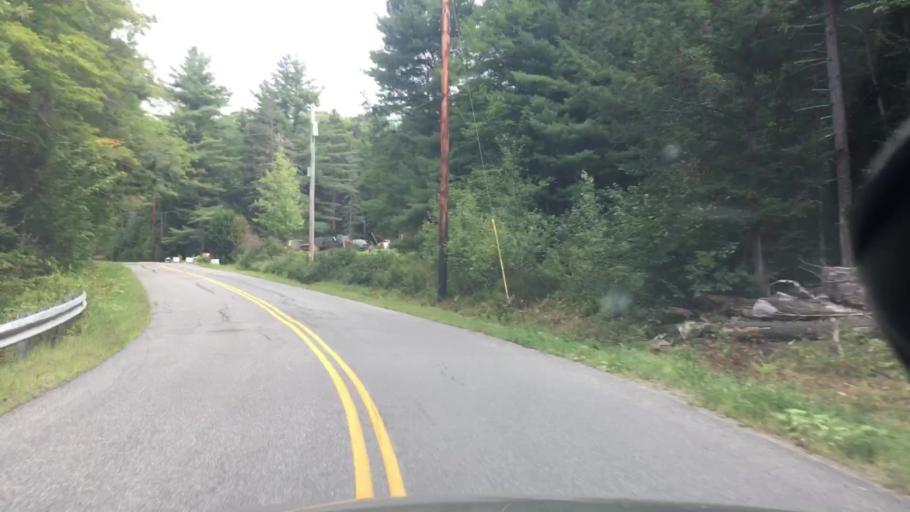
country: US
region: Vermont
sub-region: Windham County
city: Dover
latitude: 42.8053
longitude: -72.7671
